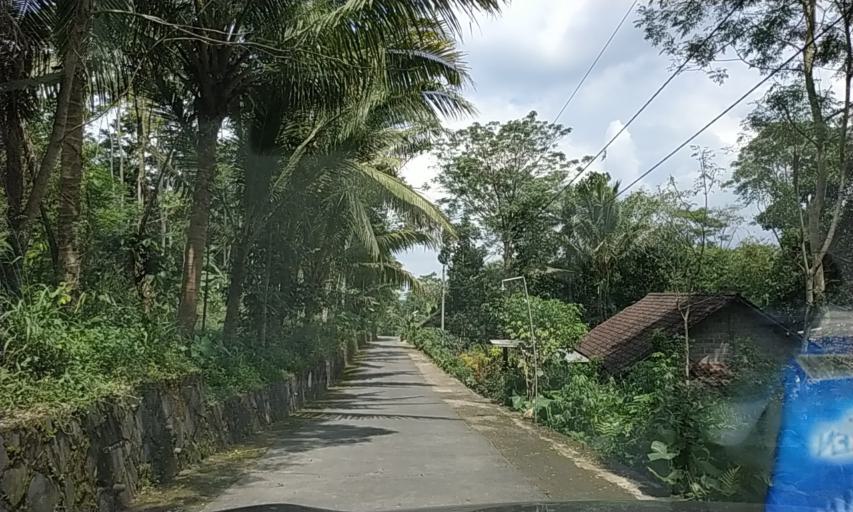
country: ID
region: Central Java
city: Jogonalan
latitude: -7.6297
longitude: 110.4820
